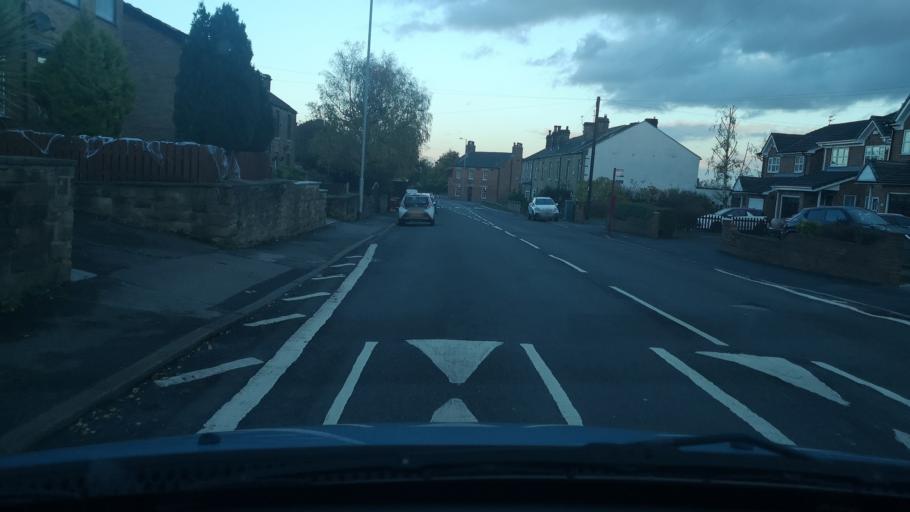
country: GB
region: England
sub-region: City and Borough of Wakefield
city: Middlestown
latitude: 53.6438
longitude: -1.5805
